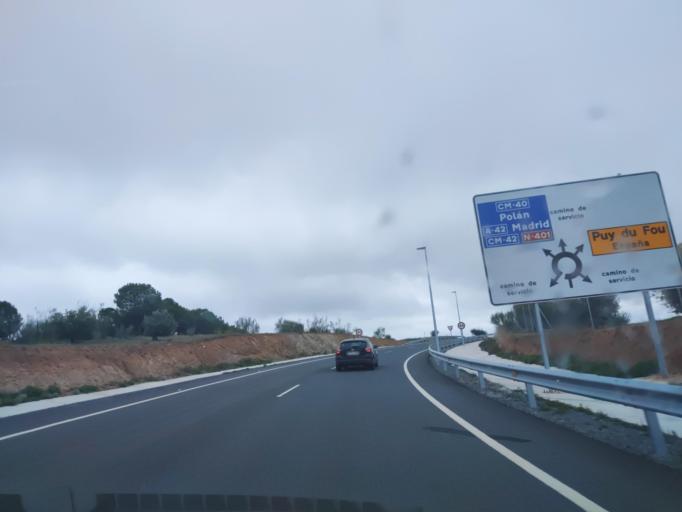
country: ES
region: Castille-La Mancha
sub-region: Province of Toledo
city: Toledo
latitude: 39.8429
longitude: -4.0877
